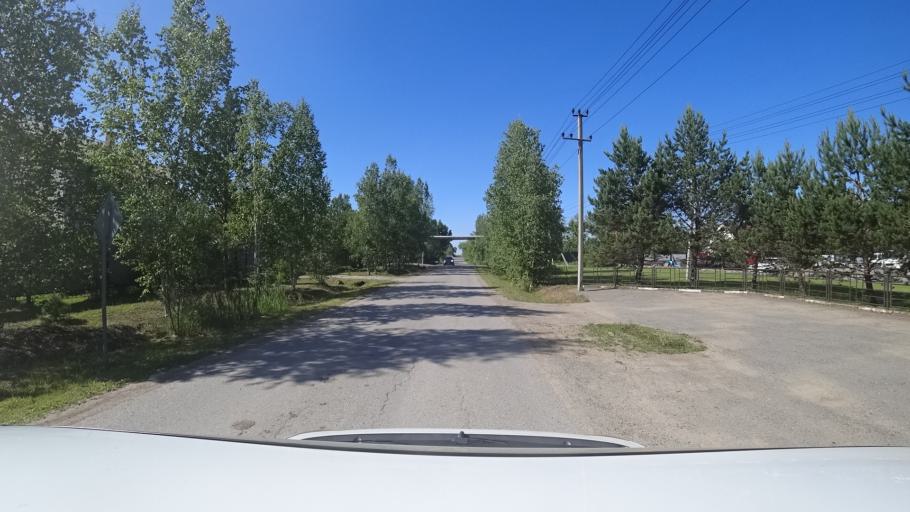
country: RU
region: Khabarovsk Krai
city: Topolevo
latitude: 48.5489
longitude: 135.1743
